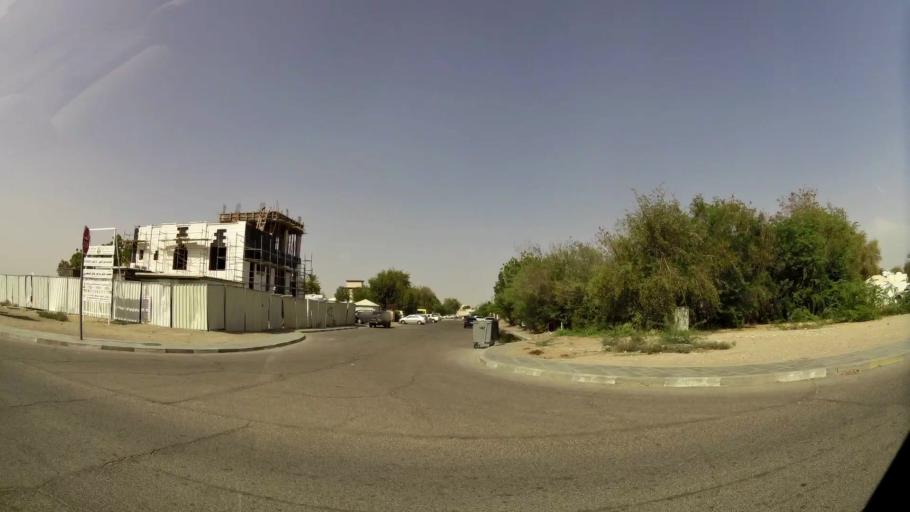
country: AE
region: Abu Dhabi
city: Al Ain
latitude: 24.2323
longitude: 55.6943
